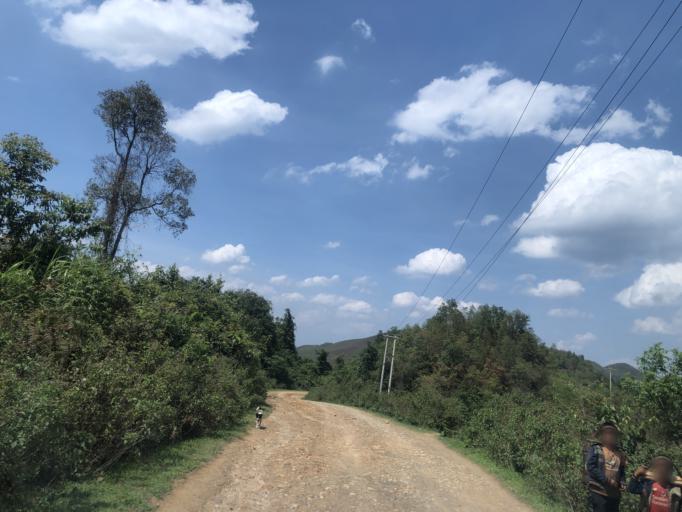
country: LA
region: Phongsali
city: Phongsali
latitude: 21.3992
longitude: 102.2257
